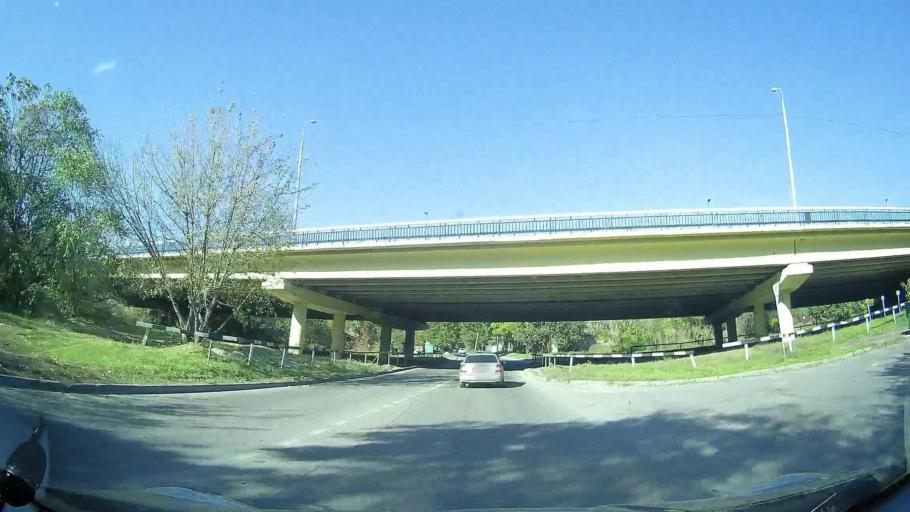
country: RU
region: Rostov
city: Rostov-na-Donu
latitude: 47.2279
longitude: 39.6717
